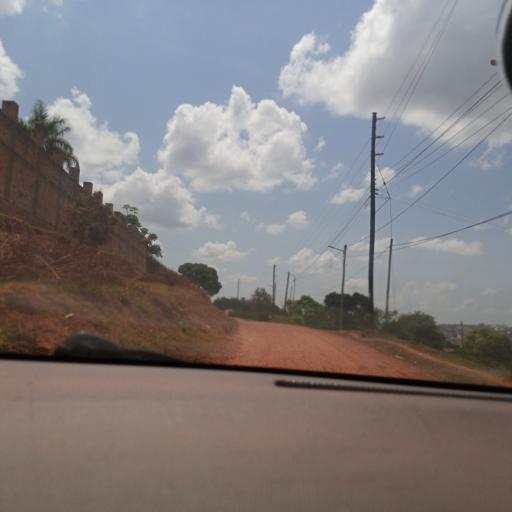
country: UG
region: Central Region
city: Masaka
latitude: -0.3273
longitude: 31.7401
